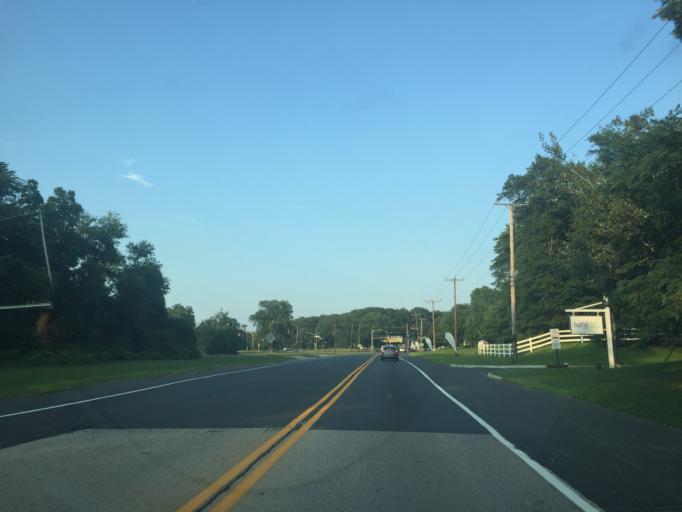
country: US
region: New Jersey
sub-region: Monmouth County
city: Wanamassa
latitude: 40.2295
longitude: -74.0636
